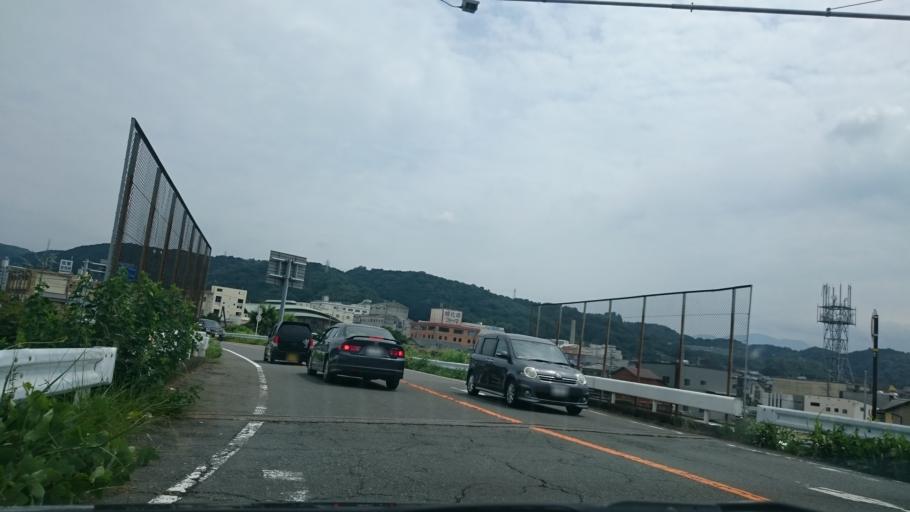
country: JP
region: Shizuoka
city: Mishima
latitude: 35.0094
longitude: 138.9442
